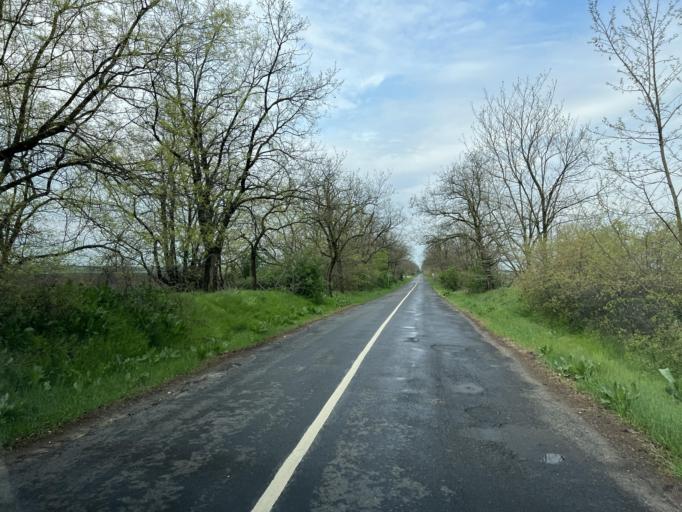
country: HU
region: Pest
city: Danszentmiklos
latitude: 47.1926
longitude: 19.5509
